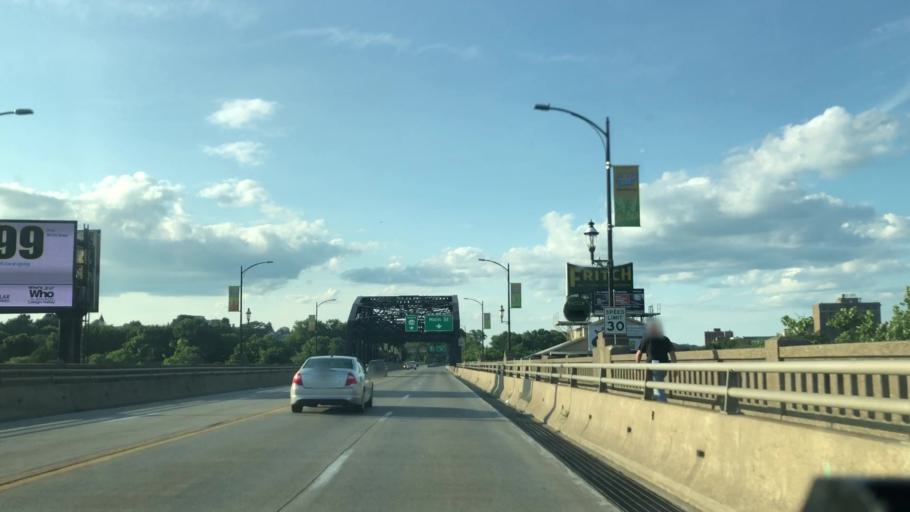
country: US
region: Pennsylvania
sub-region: Lehigh County
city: Fountain Hill
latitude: 40.6150
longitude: -75.3845
